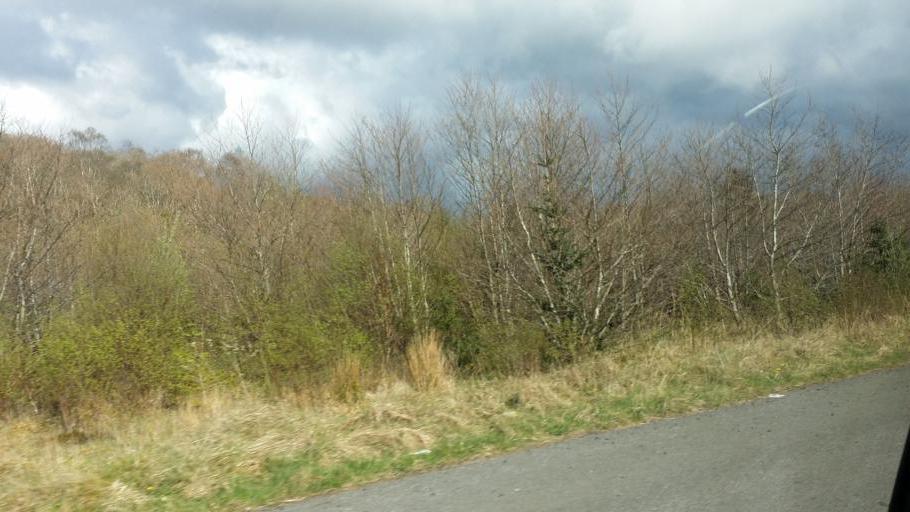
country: IE
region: Connaught
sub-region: County Leitrim
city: Manorhamilton
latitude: 54.3269
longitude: -8.2070
